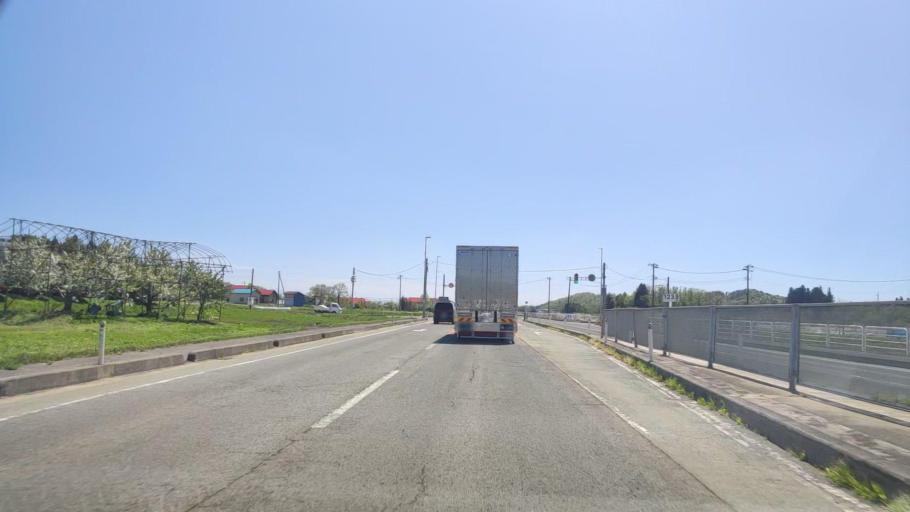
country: JP
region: Yamagata
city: Obanazawa
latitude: 38.5390
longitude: 140.3948
